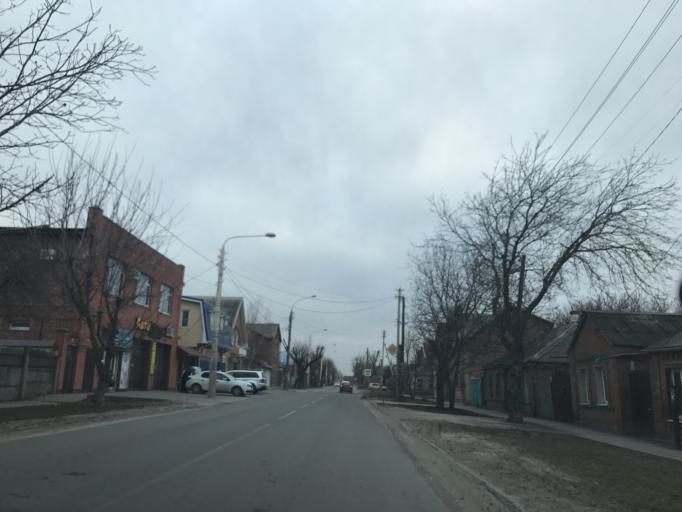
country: RU
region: Rostov
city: Rostov-na-Donu
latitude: 47.2082
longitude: 39.6637
